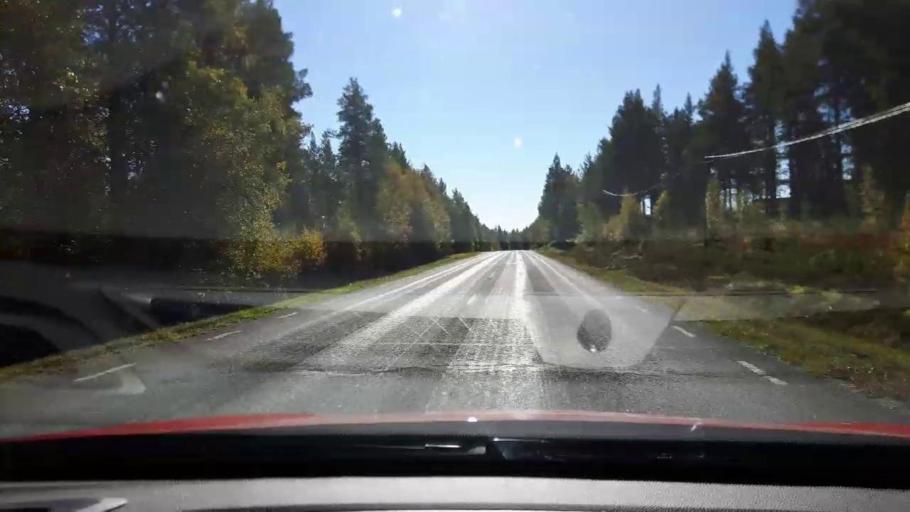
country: SE
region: Jaemtland
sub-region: Harjedalens Kommun
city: Sveg
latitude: 62.3434
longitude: 14.0368
